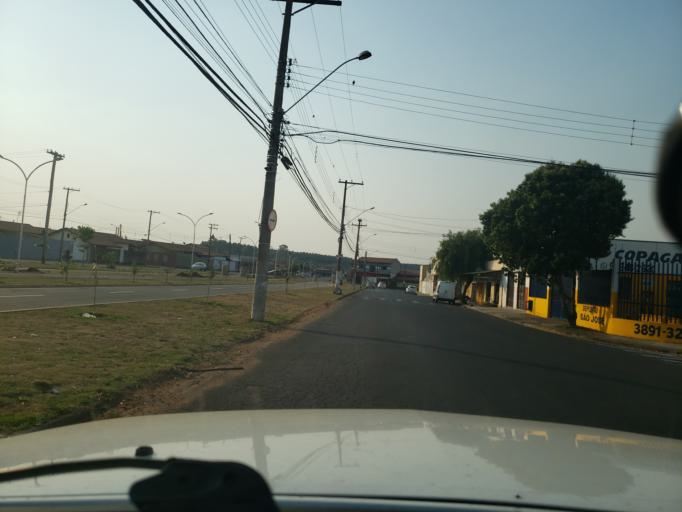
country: BR
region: Sao Paulo
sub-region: Moji-Guacu
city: Mogi-Gaucu
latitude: -22.3323
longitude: -46.9474
